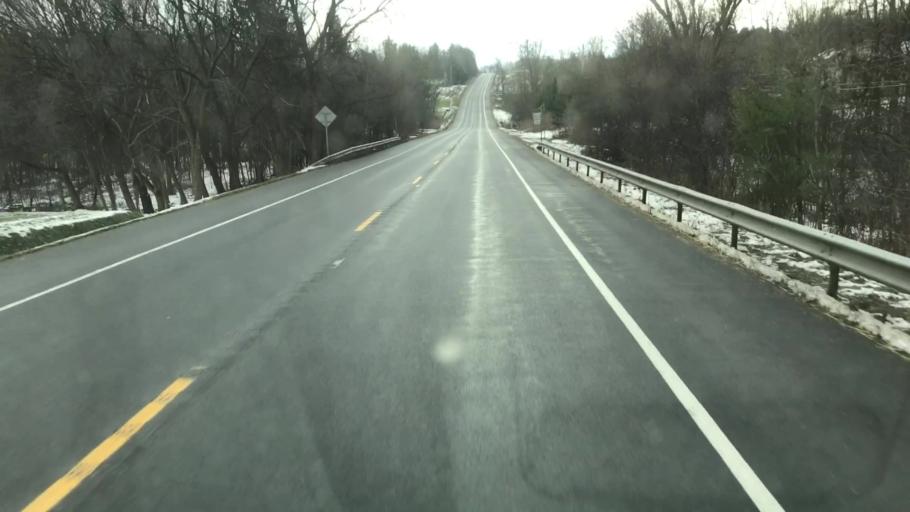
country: US
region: New York
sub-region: Onondaga County
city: Skaneateles
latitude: 42.8993
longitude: -76.4202
